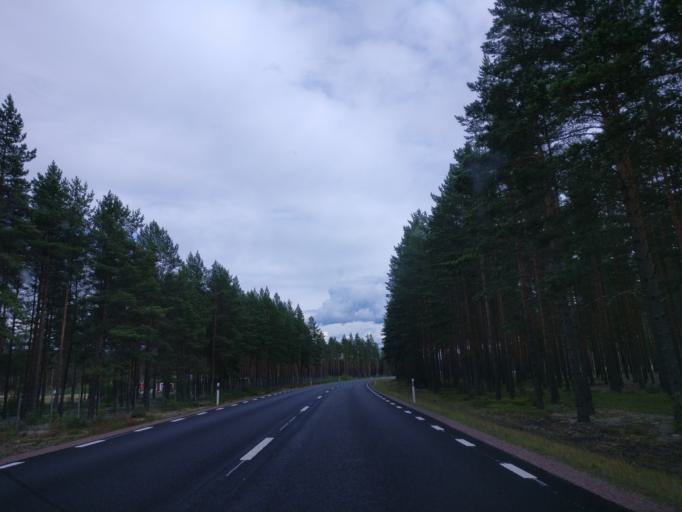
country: SE
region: Vaermland
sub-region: Hagfors Kommun
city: Hagfors
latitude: 60.0471
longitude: 13.5748
